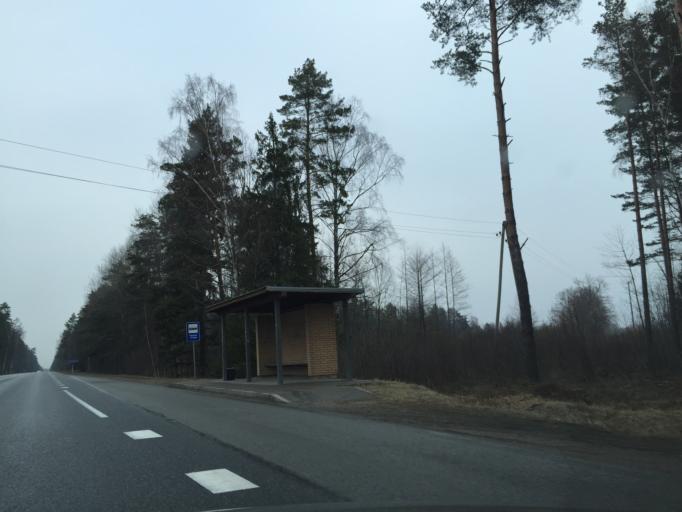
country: LV
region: Saulkrastu
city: Saulkrasti
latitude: 57.4738
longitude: 24.4343
